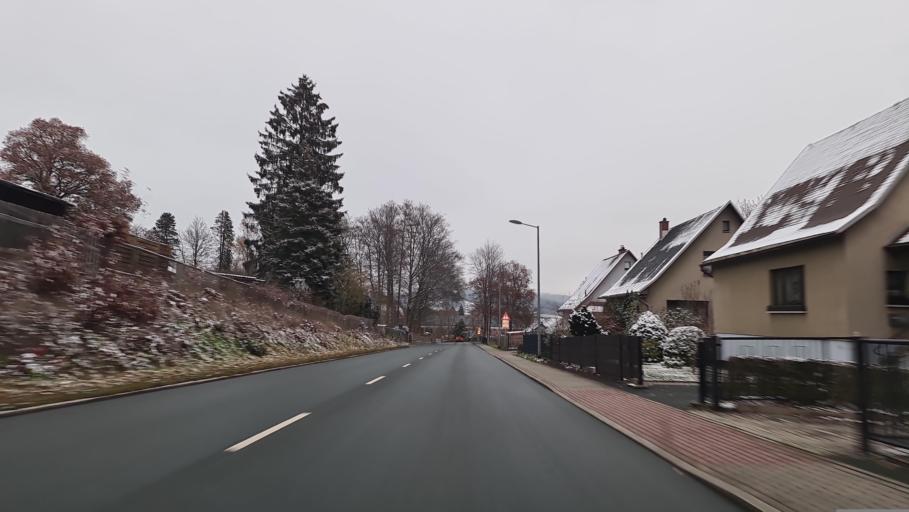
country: DE
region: Saxony
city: Markneukirchen
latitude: 50.3136
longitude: 12.3290
